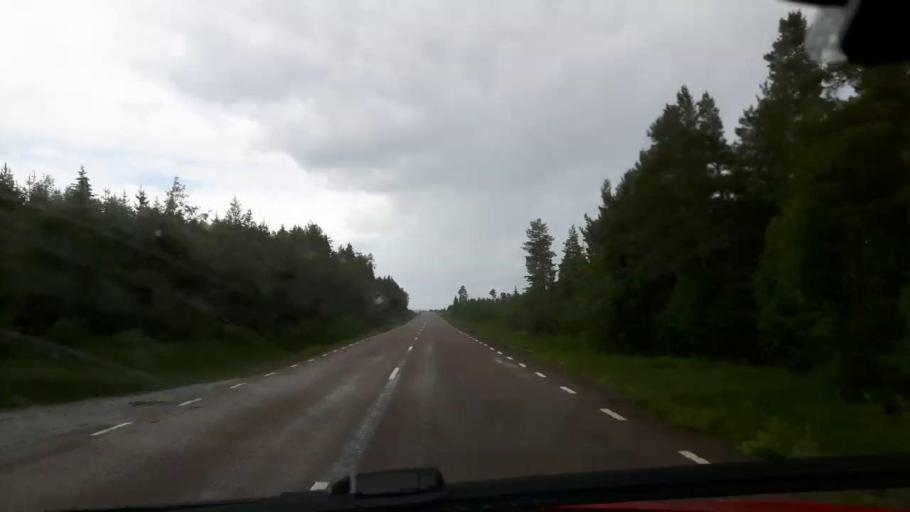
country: SE
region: Jaemtland
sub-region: Krokoms Kommun
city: Krokom
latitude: 63.8846
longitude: 14.2835
